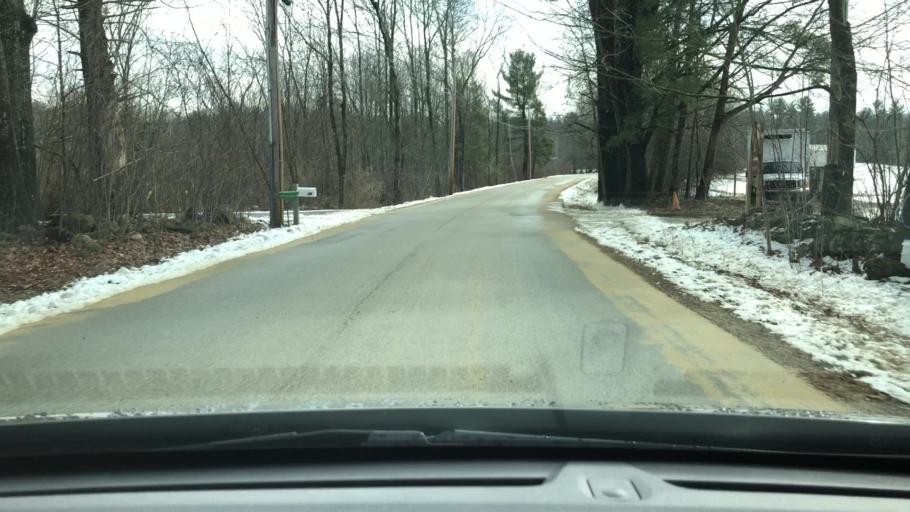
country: US
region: New Hampshire
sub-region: Strafford County
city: Madbury
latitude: 43.1857
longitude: -70.9761
